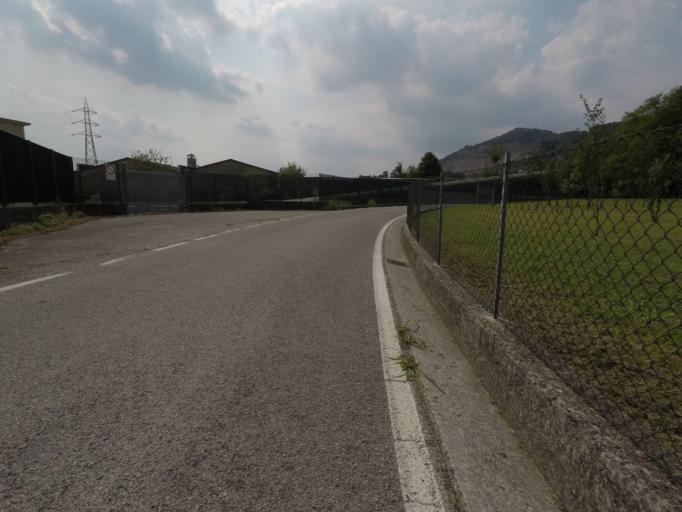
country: IT
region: Friuli Venezia Giulia
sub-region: Provincia di Pordenone
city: Caneva
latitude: 45.9677
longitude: 12.4419
